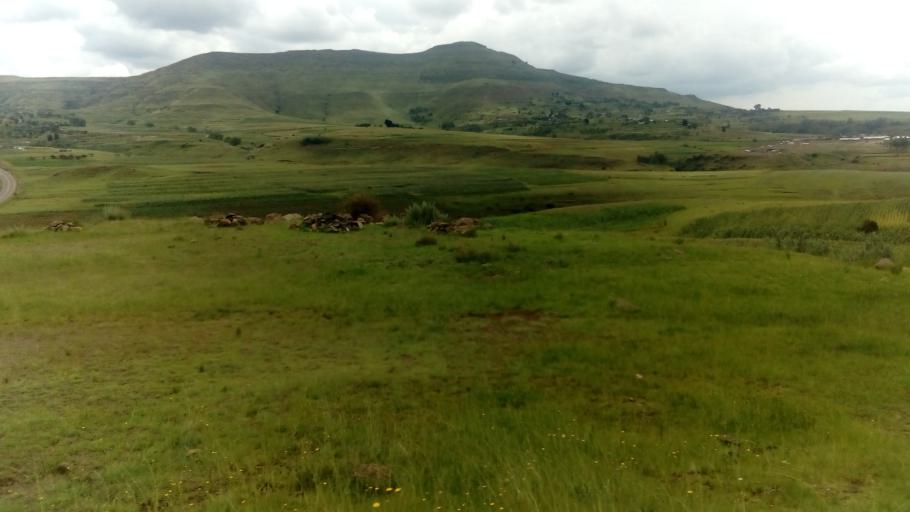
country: LS
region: Leribe
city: Leribe
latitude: -29.0355
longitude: 28.2529
